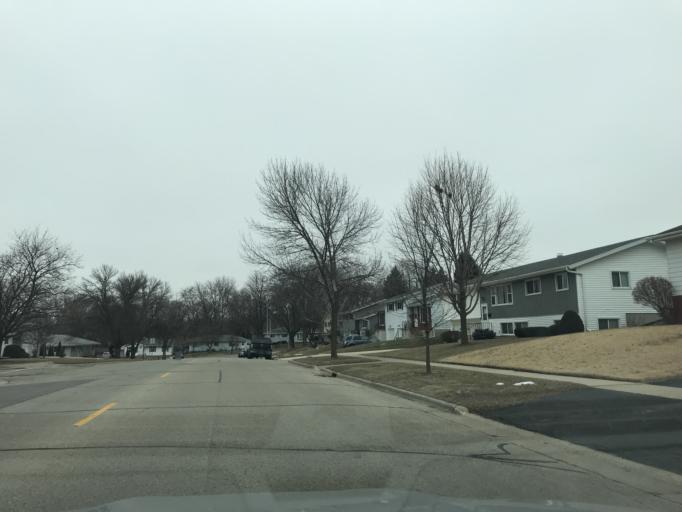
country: US
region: Wisconsin
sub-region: Dane County
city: Monona
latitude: 43.0976
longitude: -89.2984
